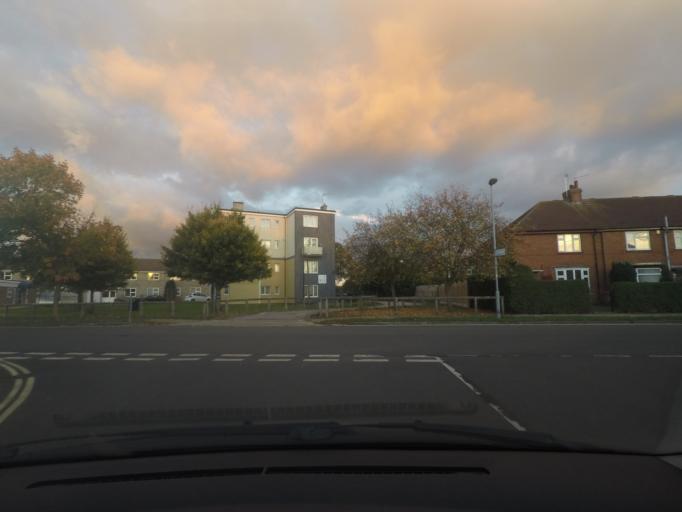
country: GB
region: England
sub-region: City of York
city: York
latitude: 53.9788
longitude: -1.0851
